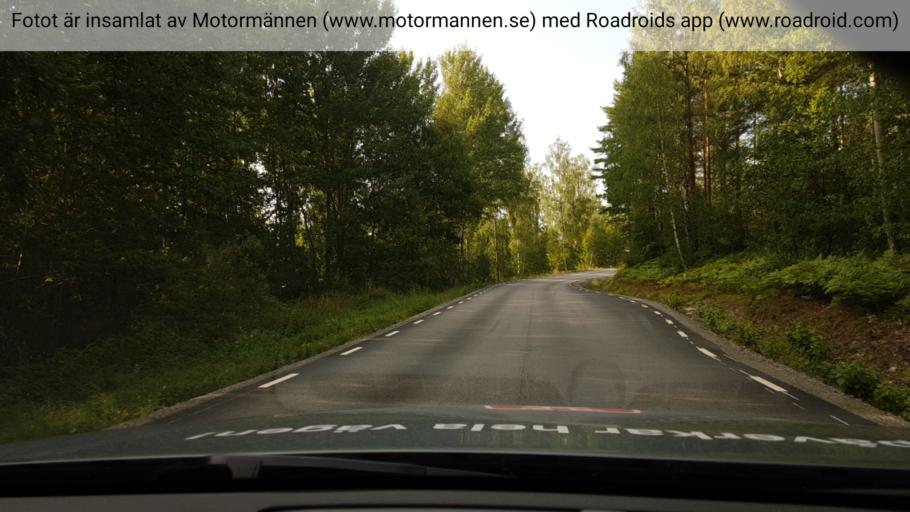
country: SE
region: Soedermanland
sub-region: Gnesta Kommun
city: Gnesta
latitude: 59.1209
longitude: 17.2164
